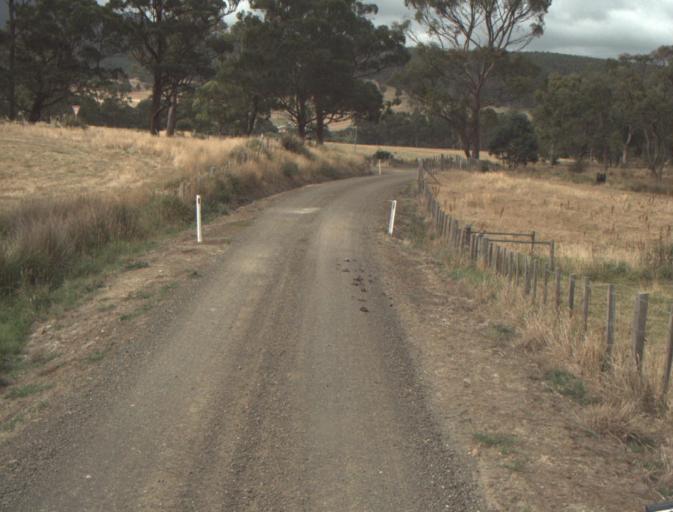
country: AU
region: Tasmania
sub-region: Dorset
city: Scottsdale
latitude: -41.4614
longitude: 147.5703
